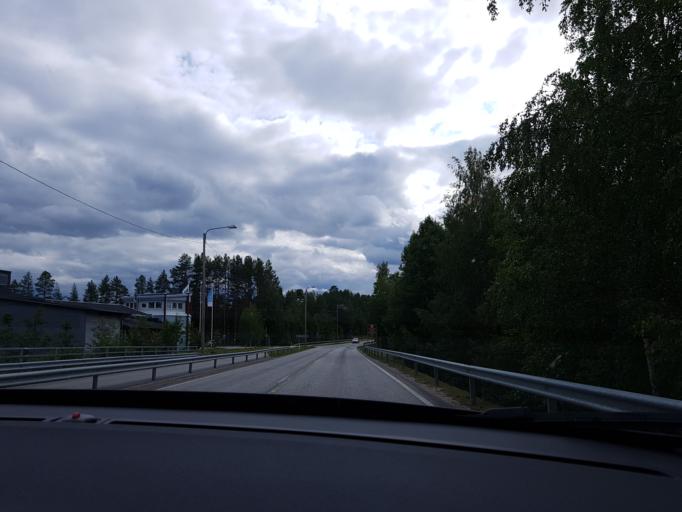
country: FI
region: Kainuu
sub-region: Kehys-Kainuu
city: Kuhmo
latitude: 64.1223
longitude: 29.5816
